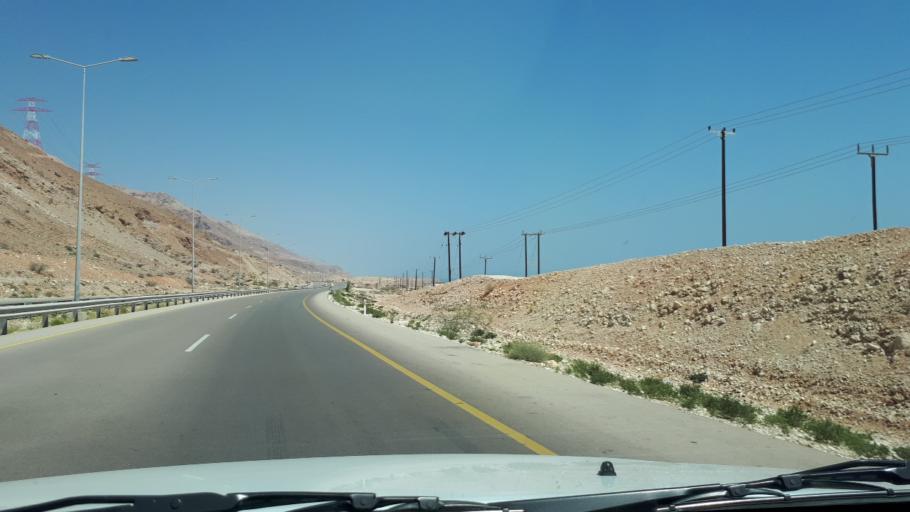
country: OM
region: Ash Sharqiyah
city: Sur
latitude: 22.7634
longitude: 59.2892
